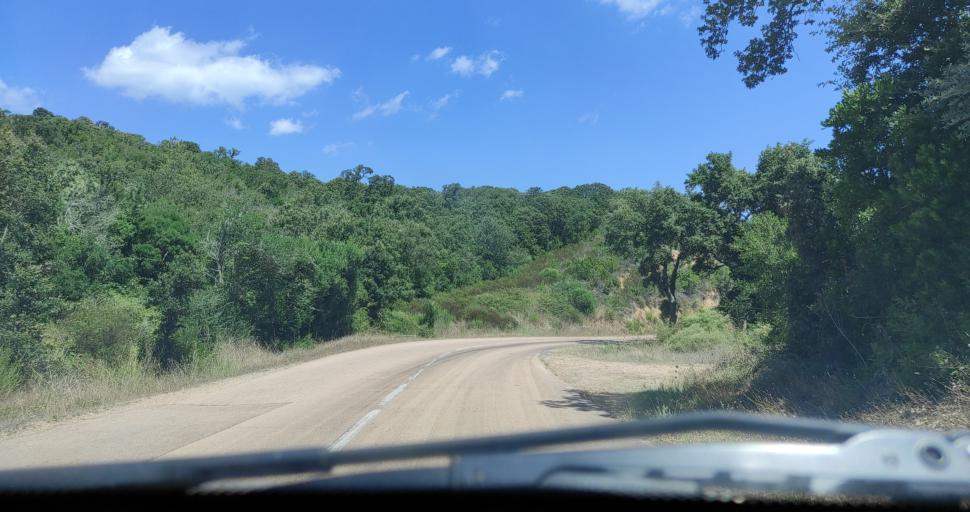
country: FR
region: Corsica
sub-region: Departement de la Corse-du-Sud
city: Porto-Vecchio
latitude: 41.5373
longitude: 9.1736
